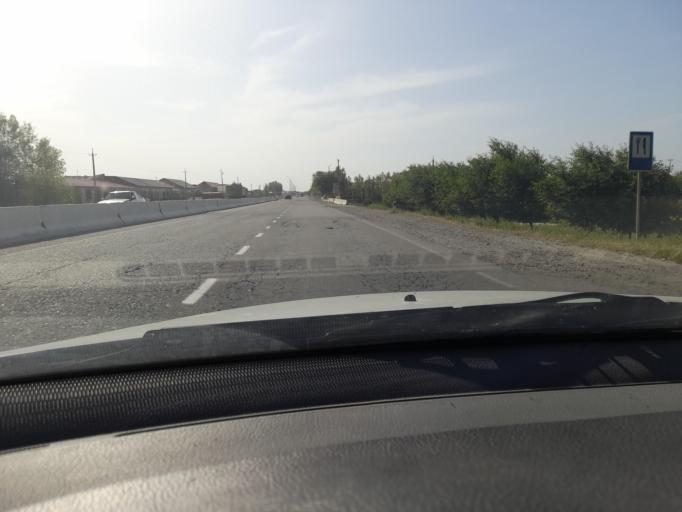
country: UZ
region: Samarqand
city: Kattaqo'rg'on
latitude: 39.9208
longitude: 66.2927
